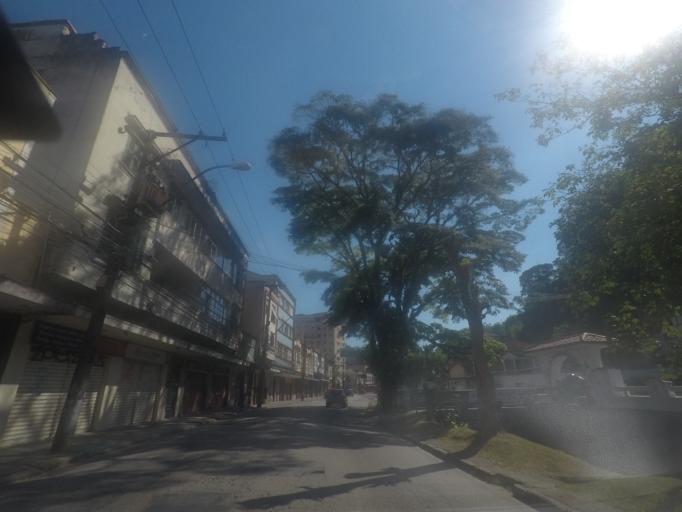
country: BR
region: Rio de Janeiro
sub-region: Petropolis
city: Petropolis
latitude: -22.5198
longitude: -43.1878
